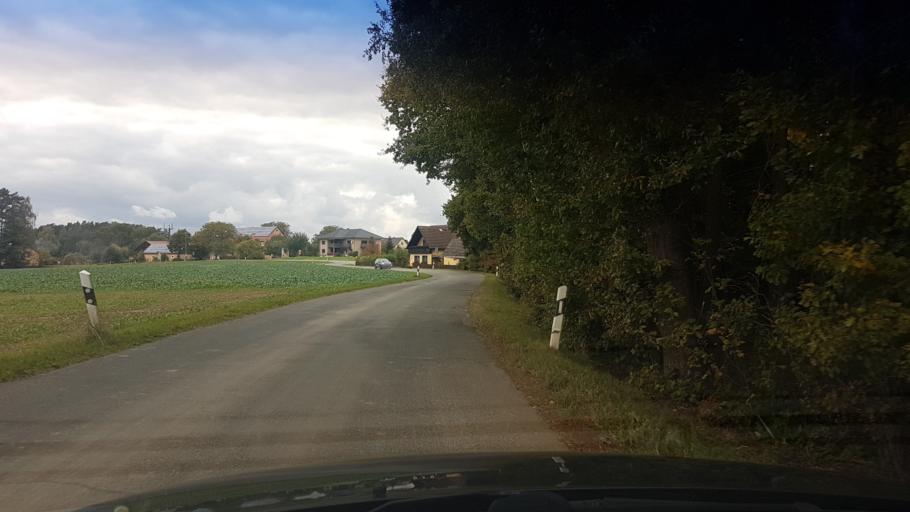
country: DE
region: Bavaria
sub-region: Upper Franconia
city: Stadelhofen
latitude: 50.0153
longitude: 11.2483
